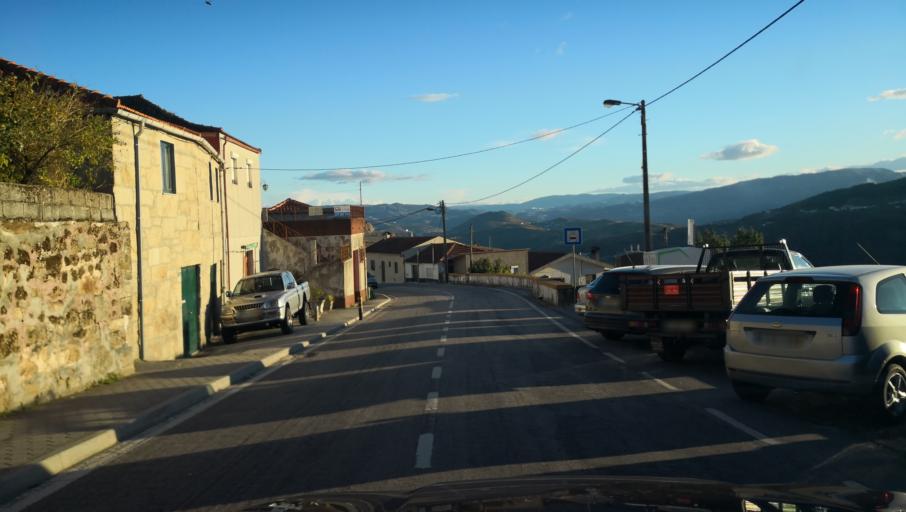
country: PT
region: Vila Real
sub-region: Santa Marta de Penaguiao
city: Santa Marta de Penaguiao
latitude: 41.2523
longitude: -7.7716
